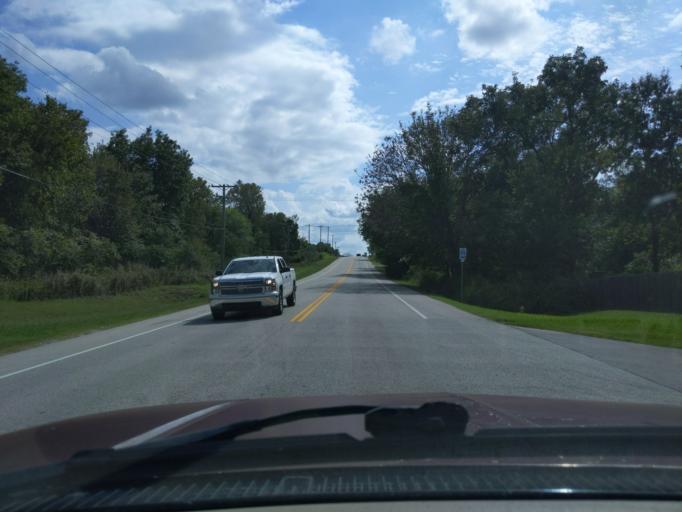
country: US
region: Oklahoma
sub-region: Tulsa County
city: Oakhurst
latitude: 36.0683
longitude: -96.0117
